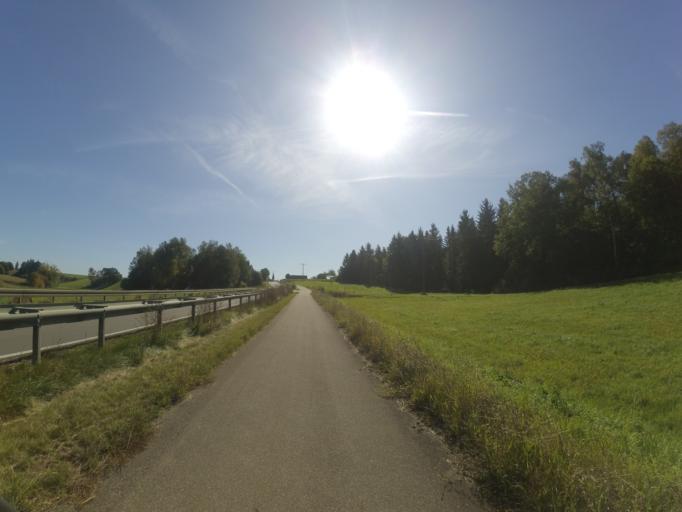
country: DE
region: Baden-Wuerttemberg
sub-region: Tuebingen Region
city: Nerenstetten
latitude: 48.5339
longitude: 10.0934
